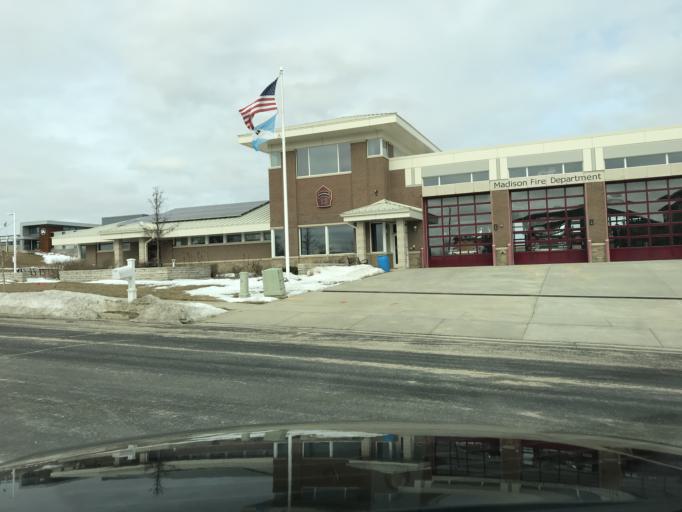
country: US
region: Wisconsin
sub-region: Dane County
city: Cottage Grove
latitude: 43.1013
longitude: -89.2695
